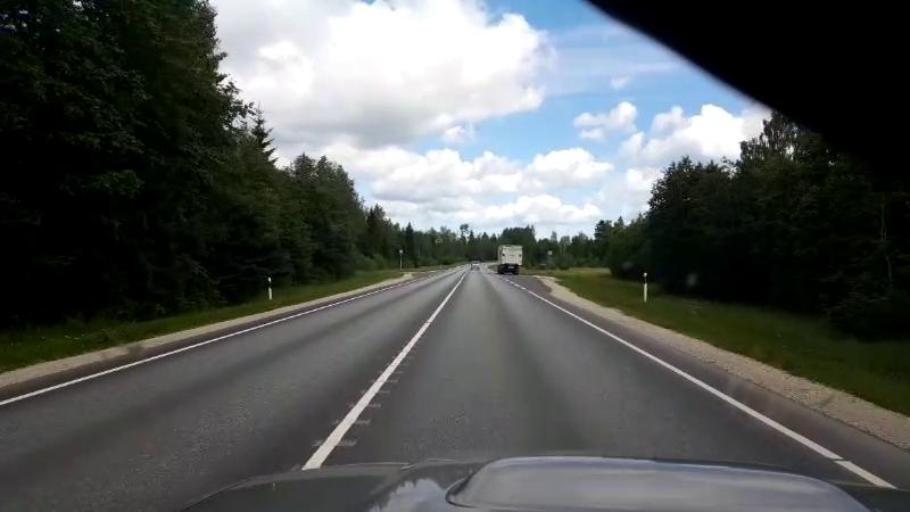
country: EE
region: Laeaene-Virumaa
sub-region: Tapa vald
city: Tapa
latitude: 59.2783
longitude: 26.0407
